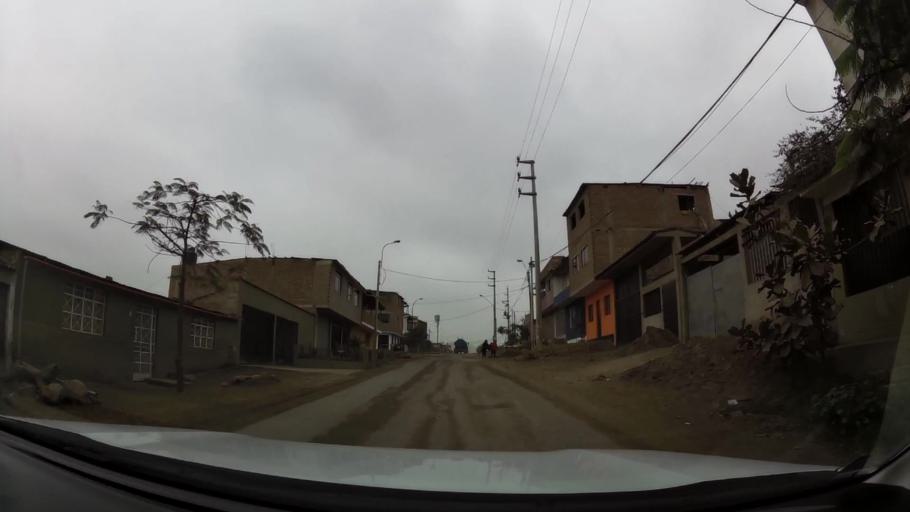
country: PE
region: Lima
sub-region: Lima
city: Cieneguilla
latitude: -12.2176
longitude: -76.9015
